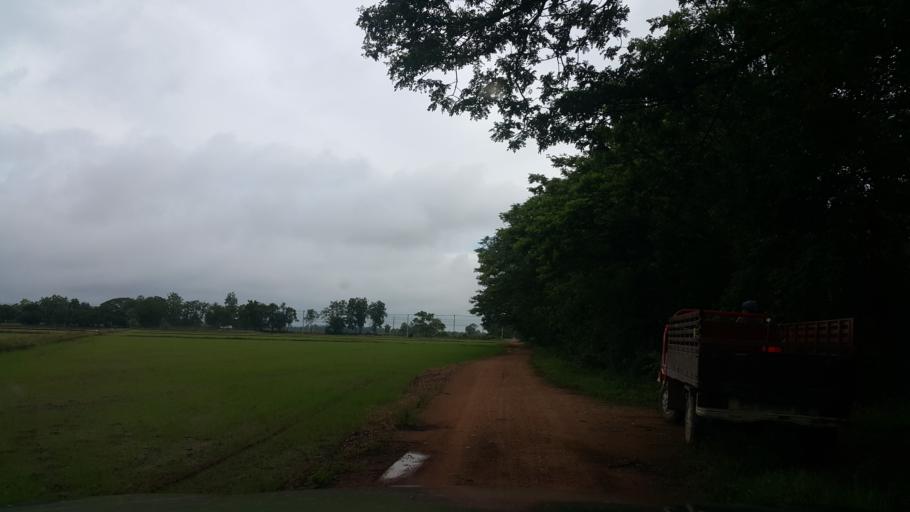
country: TH
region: Sukhothai
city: Sawankhalok
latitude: 17.3070
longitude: 99.7136
